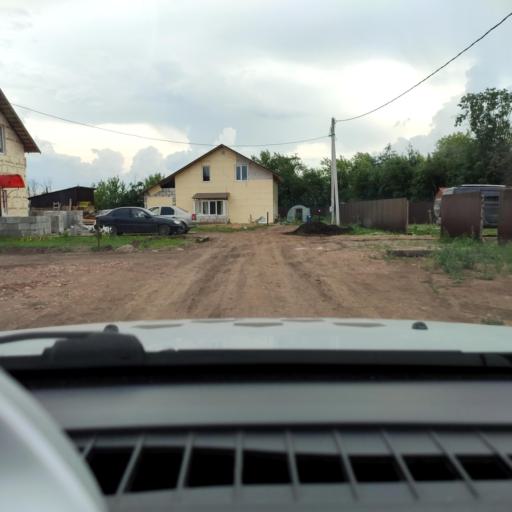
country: RU
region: Perm
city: Froly
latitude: 57.9204
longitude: 56.2590
